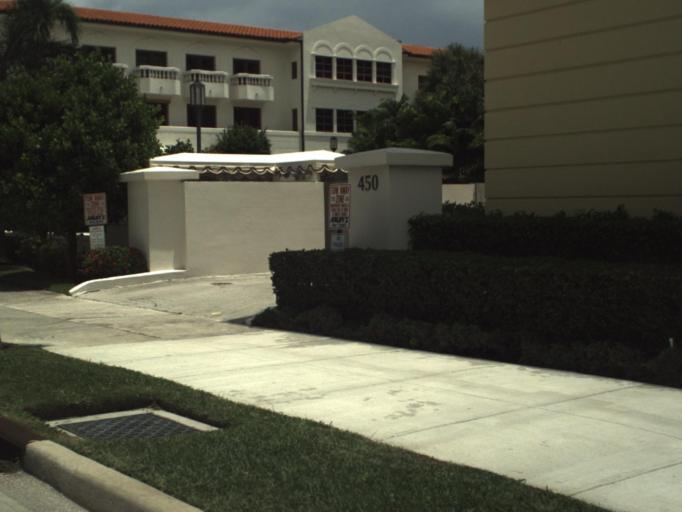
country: US
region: Florida
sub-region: Palm Beach County
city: Palm Beach
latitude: 26.7057
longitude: -80.0433
